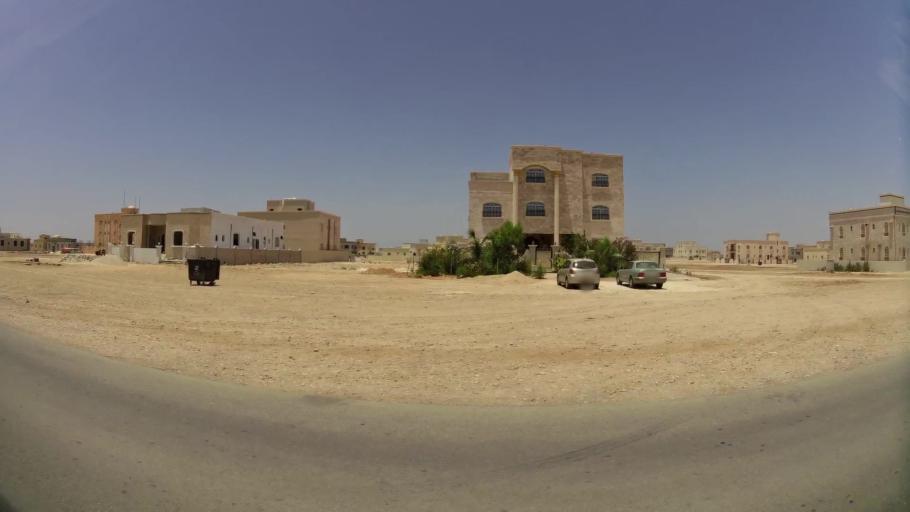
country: OM
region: Zufar
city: Salalah
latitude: 17.0919
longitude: 54.2090
